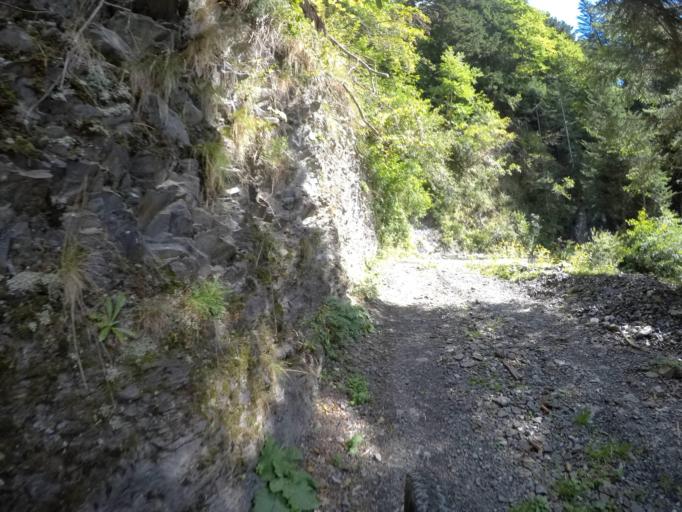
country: IT
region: Friuli Venezia Giulia
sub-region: Provincia di Udine
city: Paularo
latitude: 46.5629
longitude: 13.1301
